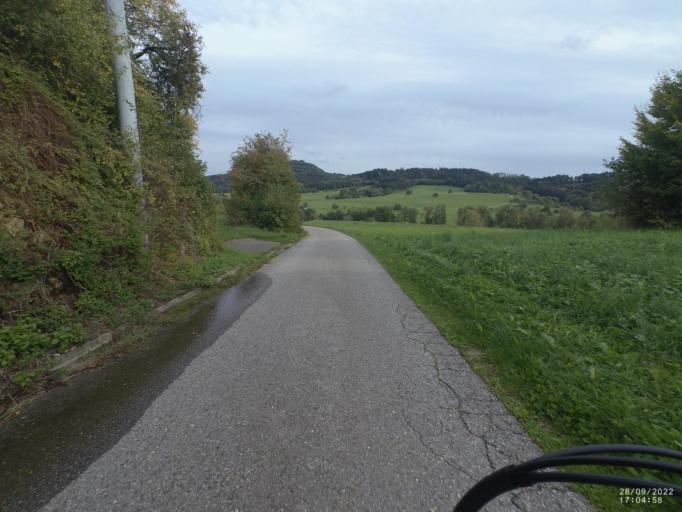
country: DE
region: Baden-Wuerttemberg
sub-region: Regierungsbezirk Stuttgart
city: Waschenbeuren
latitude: 48.7549
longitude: 9.6898
